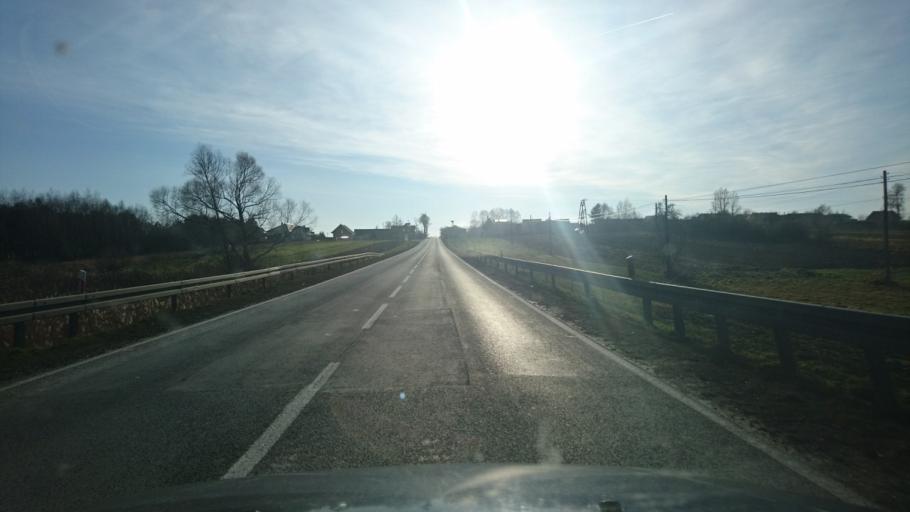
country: PL
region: Opole Voivodeship
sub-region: Powiat oleski
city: Dalachow
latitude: 51.0550
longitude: 18.5990
